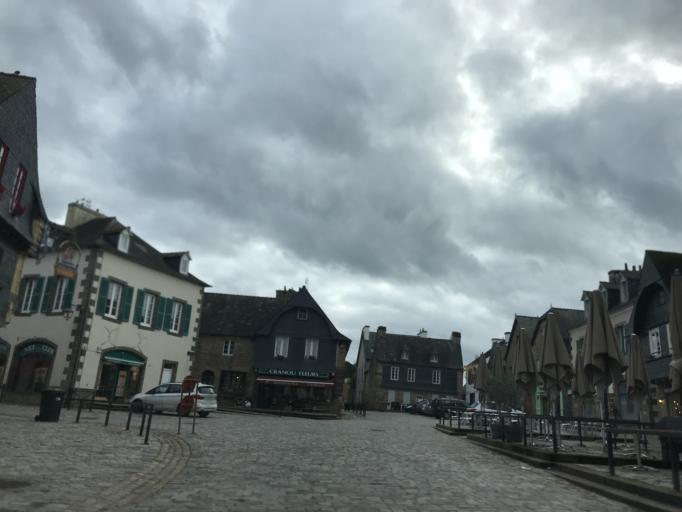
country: FR
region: Brittany
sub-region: Departement du Finistere
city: Le Faou
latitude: 48.2947
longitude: -4.1797
